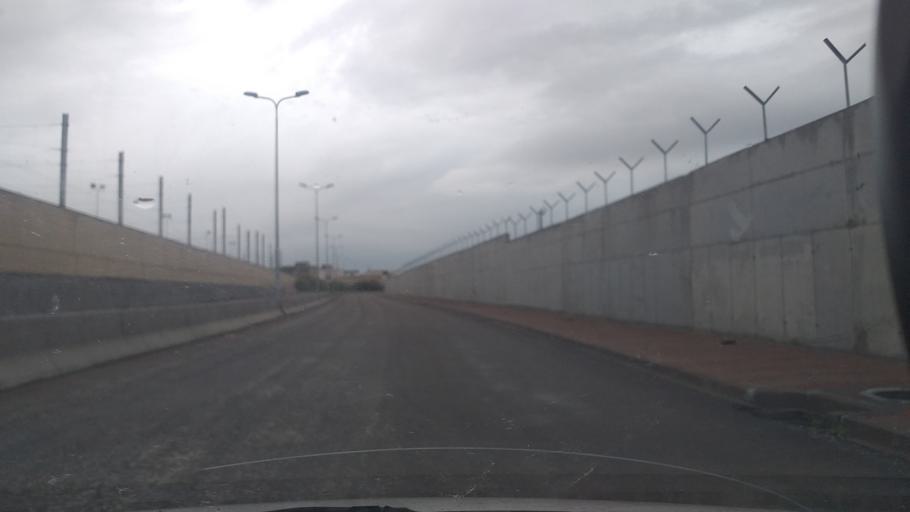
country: TN
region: Ariana
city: Ariana
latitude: 36.8577
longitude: 10.2139
